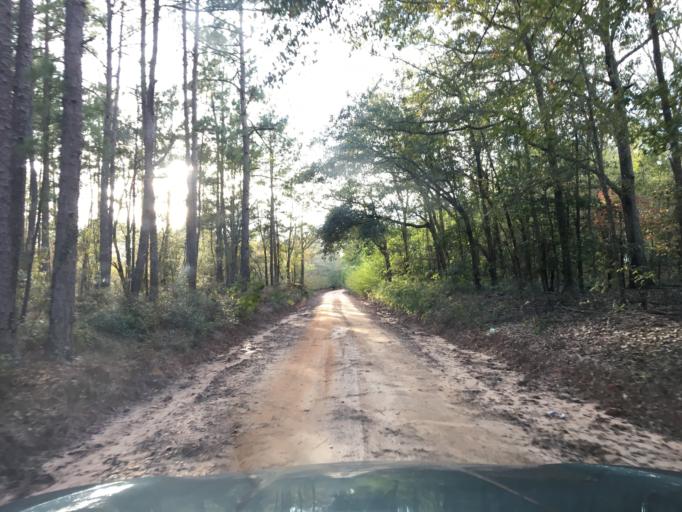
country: US
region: South Carolina
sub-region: Barnwell County
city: Williston
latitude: 33.6663
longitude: -81.3685
